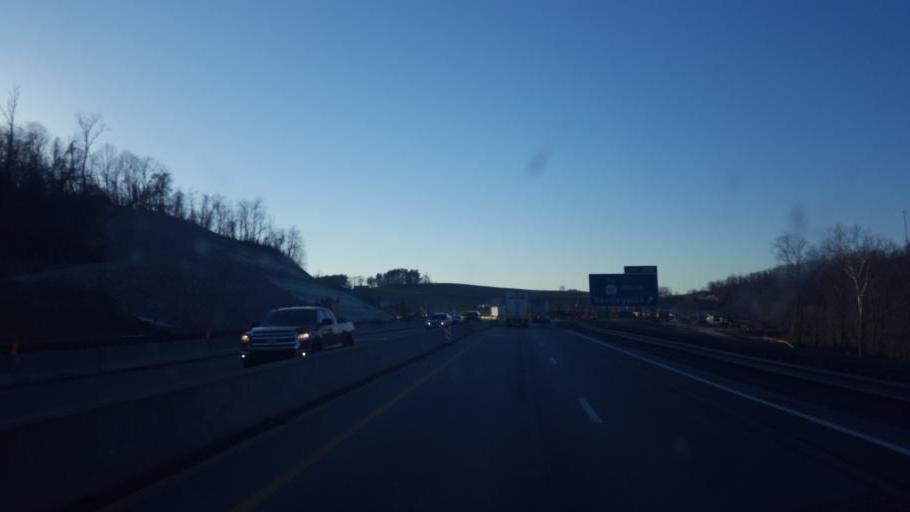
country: US
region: Pennsylvania
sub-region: Washington County
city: Bentleyville
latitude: 40.1316
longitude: -79.9916
